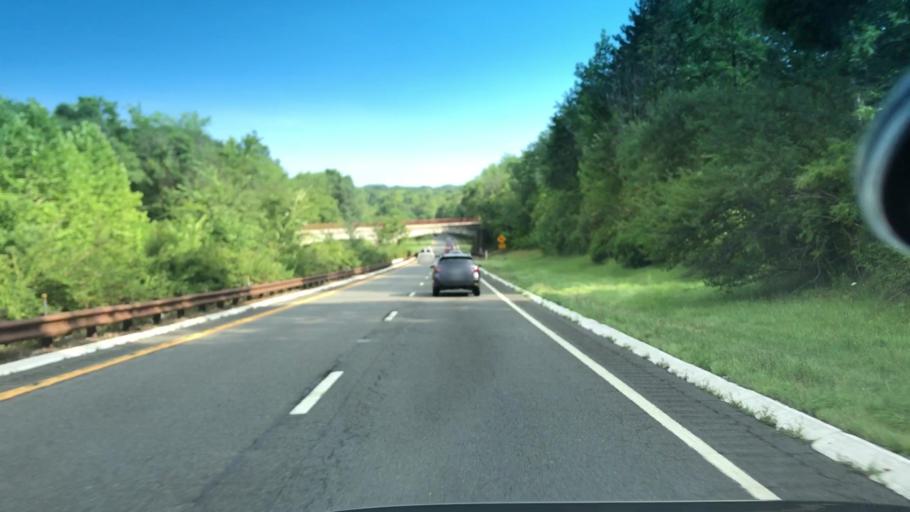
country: US
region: New York
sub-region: Rockland County
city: Blauvelt
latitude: 41.0709
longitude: -73.9811
